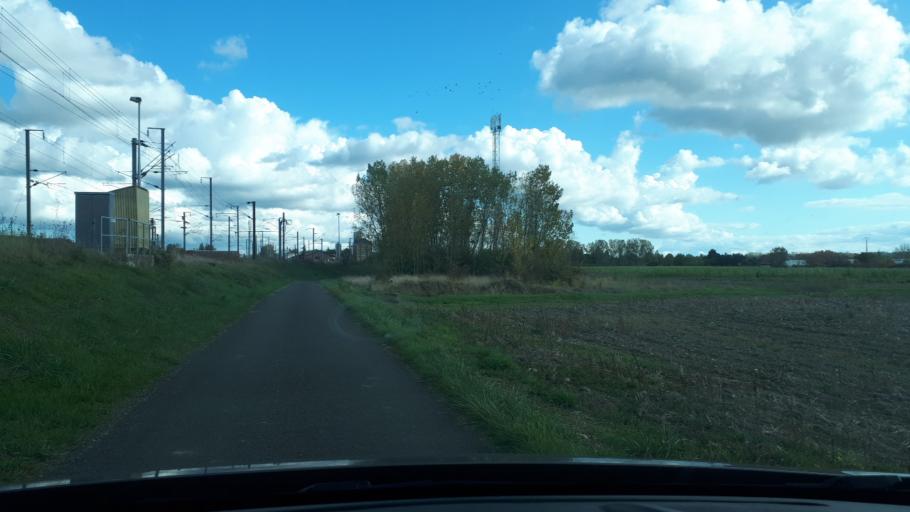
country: FR
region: Centre
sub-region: Departement du Loir-et-Cher
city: Saint-Aignan
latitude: 47.2895
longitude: 1.3777
